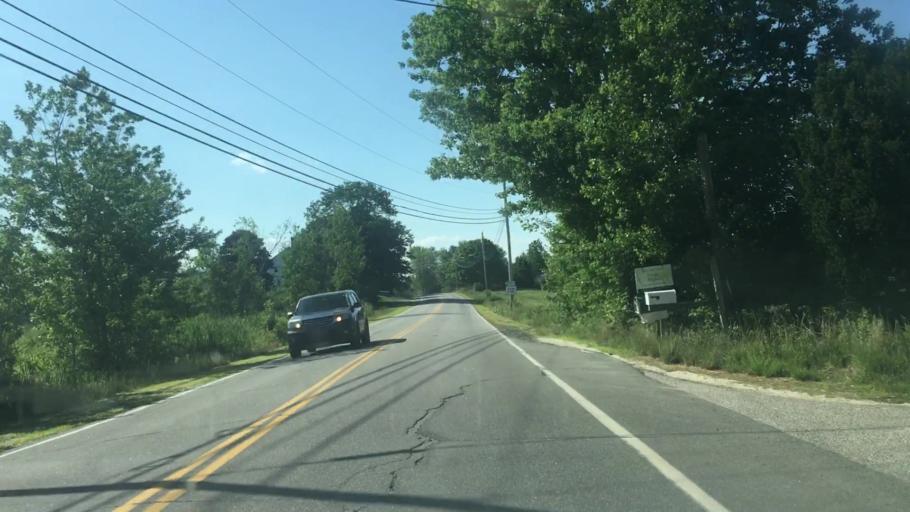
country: US
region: Maine
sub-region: York County
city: Buxton
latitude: 43.6253
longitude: -70.5492
